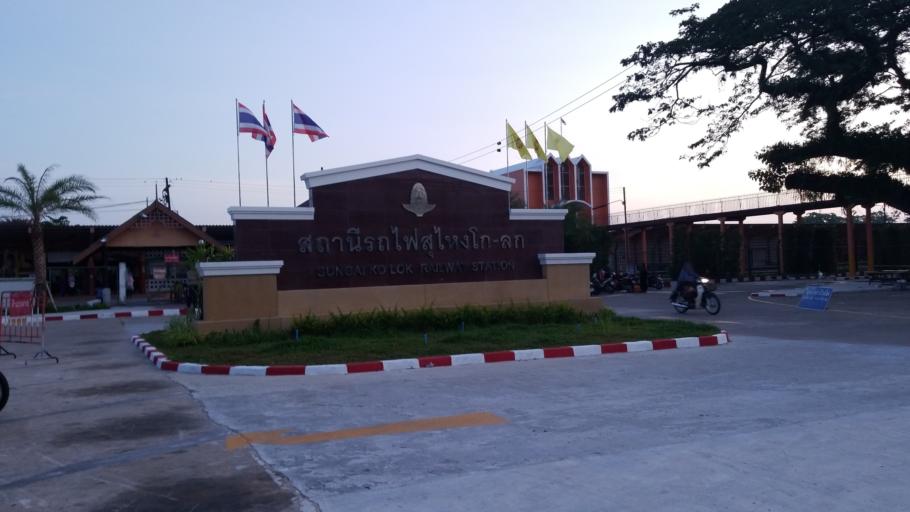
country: TH
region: Narathiwat
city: Su-ngai Kolok
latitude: 6.0253
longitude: 101.9646
